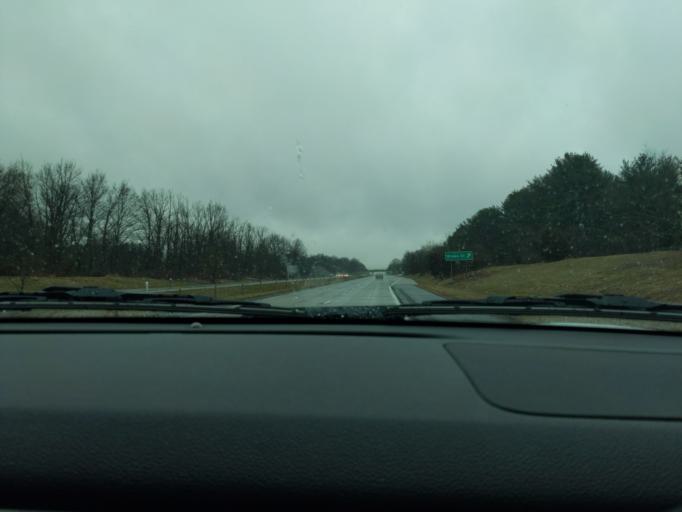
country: US
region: Pennsylvania
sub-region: Bucks County
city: Doylestown
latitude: 40.3155
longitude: -75.1465
